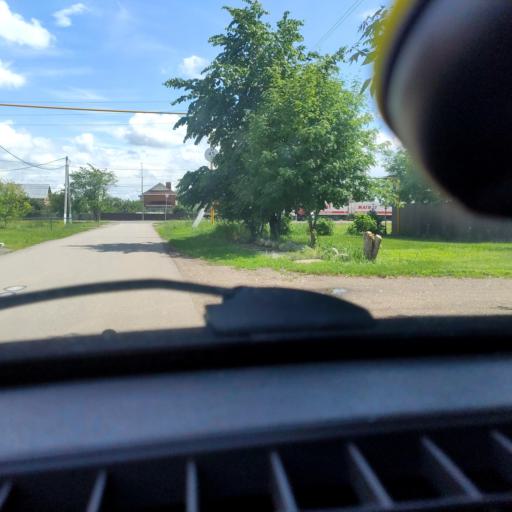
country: RU
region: Samara
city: Zhigulevsk
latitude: 53.5497
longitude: 49.5227
